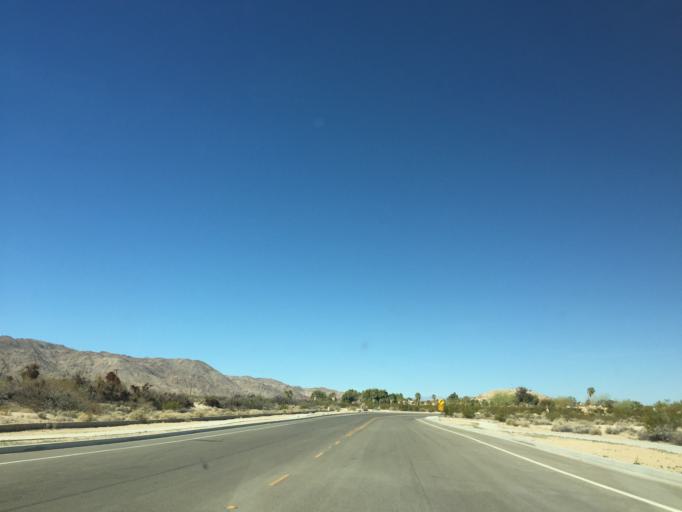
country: US
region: California
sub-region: San Bernardino County
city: Twentynine Palms
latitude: 34.1294
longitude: -116.0429
